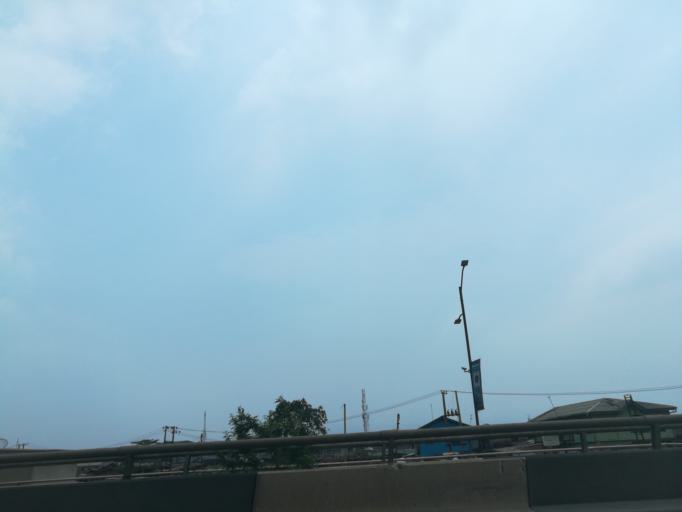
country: NG
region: Lagos
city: Somolu
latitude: 6.5436
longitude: 3.3989
